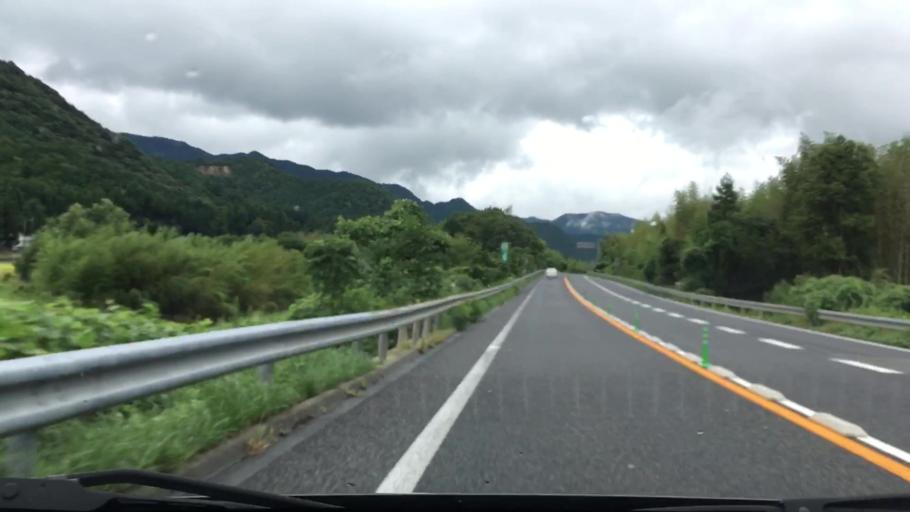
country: JP
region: Hyogo
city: Nishiwaki
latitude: 35.0894
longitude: 134.7772
